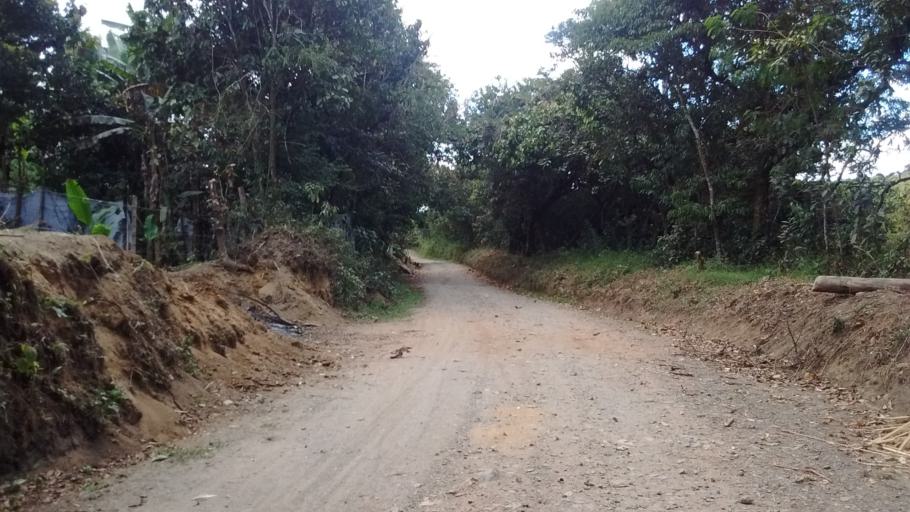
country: CO
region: Cauca
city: Popayan
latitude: 2.4920
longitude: -76.5865
